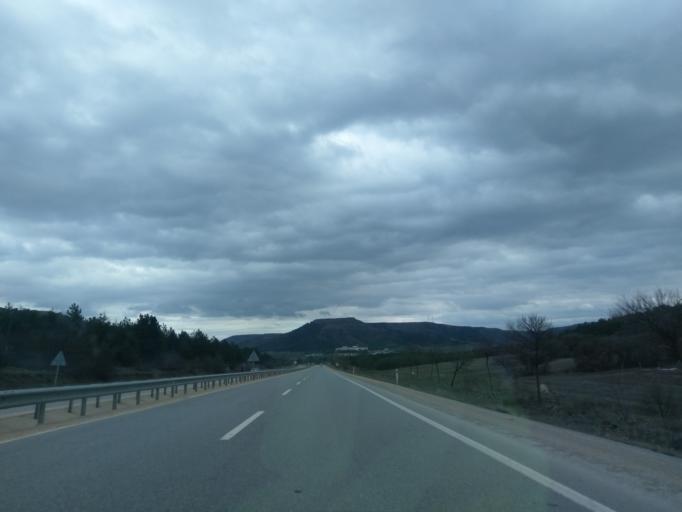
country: TR
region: Eskisehir
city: Eskisehir
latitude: 39.7417
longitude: 30.4154
